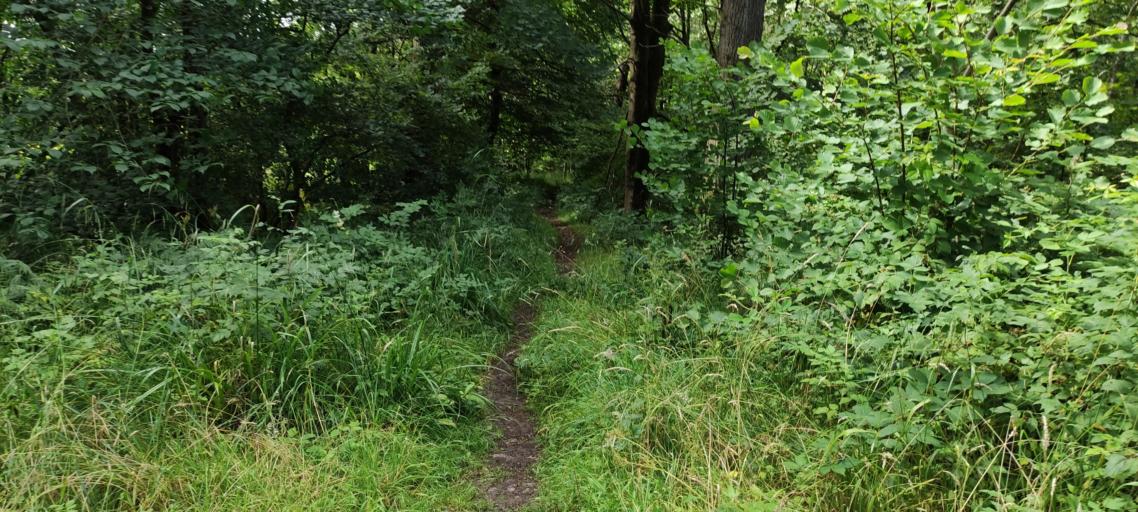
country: GB
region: England
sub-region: Cumbria
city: Cockermouth
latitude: 54.6638
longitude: -3.2398
